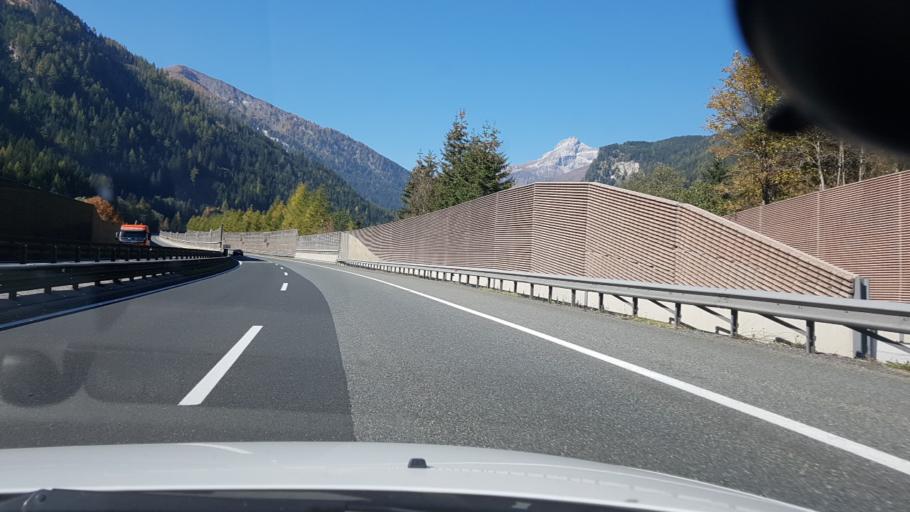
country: AT
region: Salzburg
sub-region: Politischer Bezirk Tamsweg
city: Zederhaus
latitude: 47.1631
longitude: 13.4780
